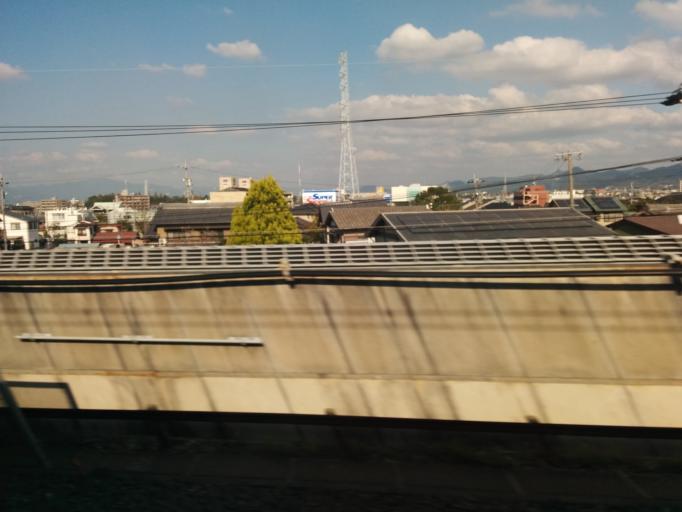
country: JP
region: Aichi
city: Toyohashi
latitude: 34.7452
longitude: 137.3946
